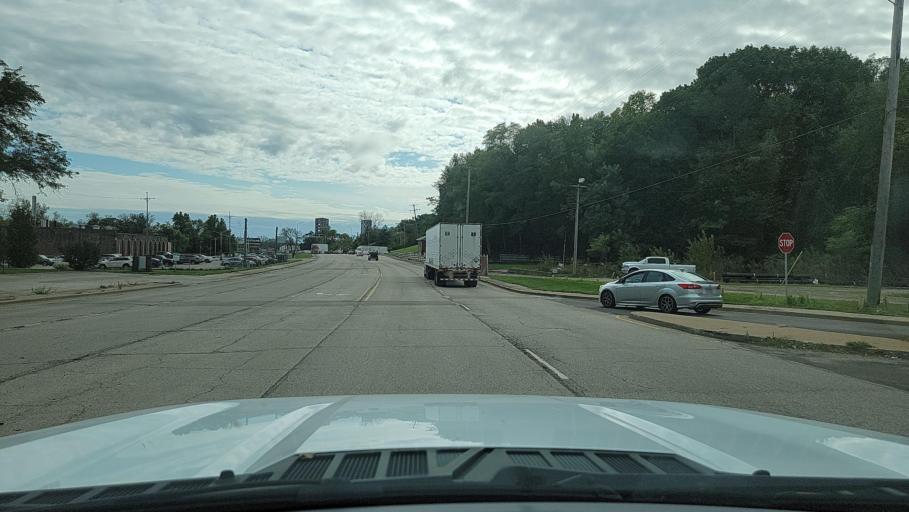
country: US
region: Illinois
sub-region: Peoria County
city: Bartonville
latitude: 40.6417
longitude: -89.6520
